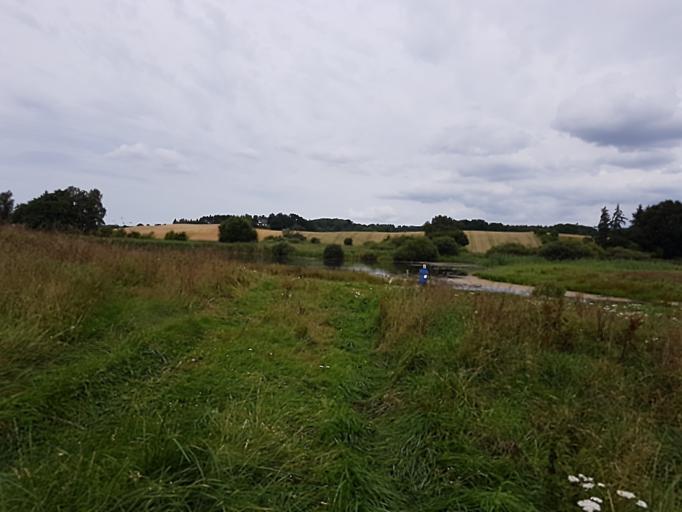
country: DK
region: Capital Region
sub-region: Egedal Kommune
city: Stenlose
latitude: 55.7981
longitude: 12.1959
